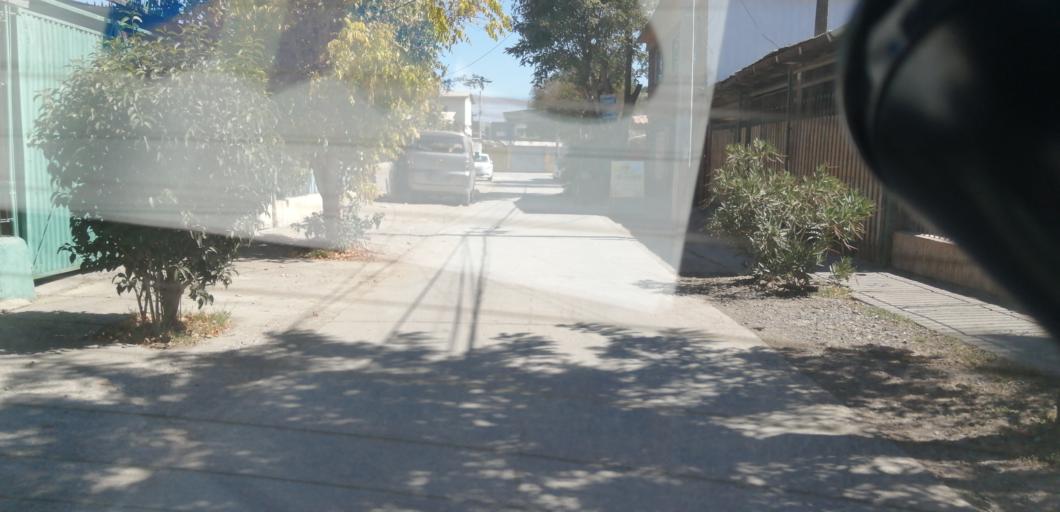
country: CL
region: Santiago Metropolitan
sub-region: Provincia de Santiago
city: Lo Prado
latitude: -33.4320
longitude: -70.7630
